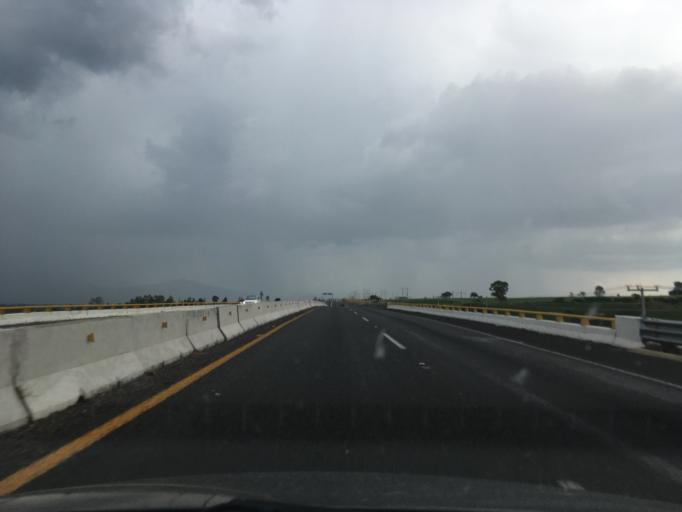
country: MX
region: Guanajuato
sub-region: Tarimoro
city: San Juan Bautista Cacalote
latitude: 20.3460
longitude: -100.8051
